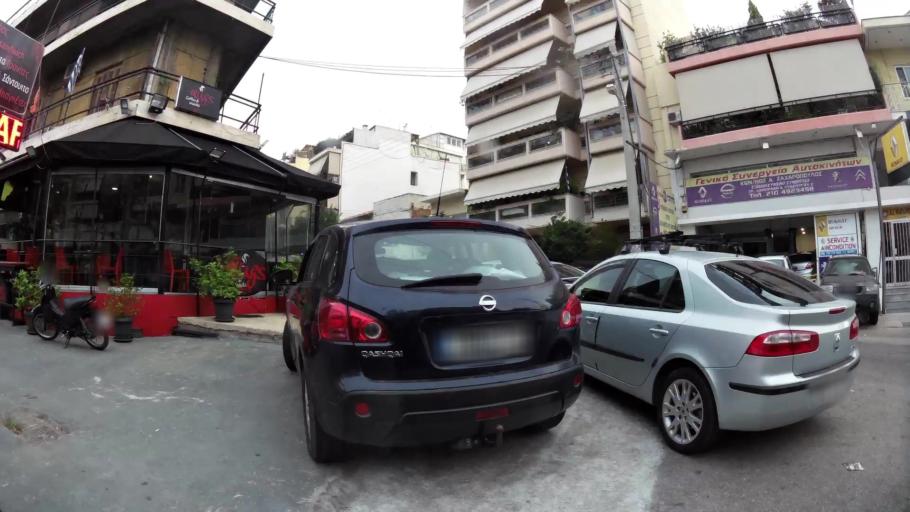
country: GR
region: Attica
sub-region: Nomos Piraios
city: Korydallos
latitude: 37.9788
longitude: 23.6388
